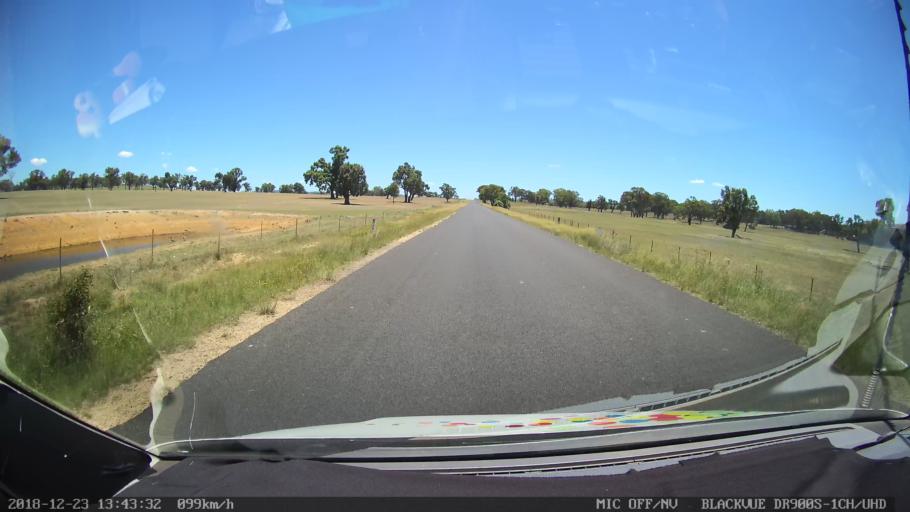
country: AU
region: New South Wales
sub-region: Tamworth Municipality
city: Manilla
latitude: -30.4868
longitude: 151.1484
